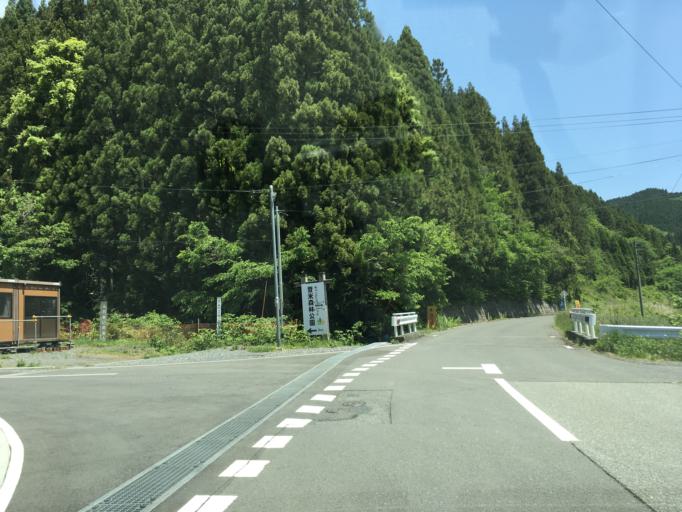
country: JP
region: Miyagi
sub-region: Oshika Gun
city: Onagawa Cho
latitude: 38.6730
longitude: 141.3472
